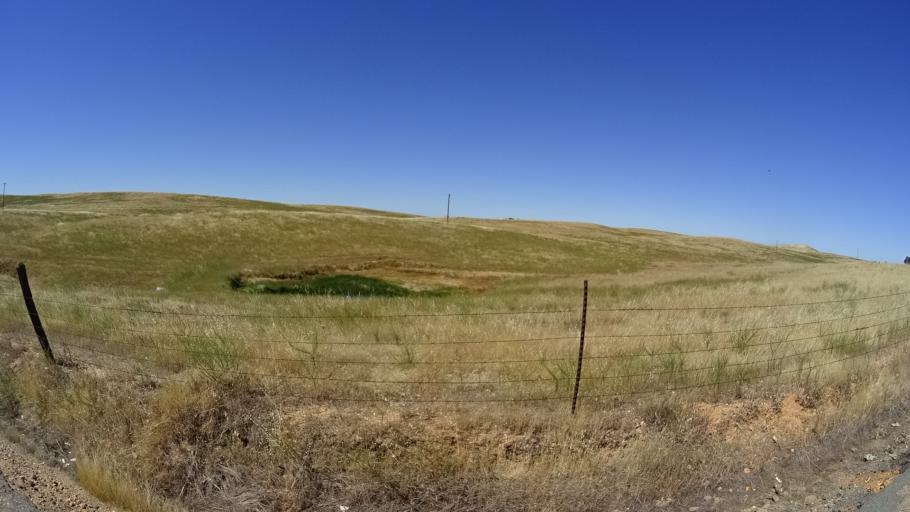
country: US
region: California
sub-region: Calaveras County
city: Rancho Calaveras
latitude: 38.0278
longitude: -120.8466
